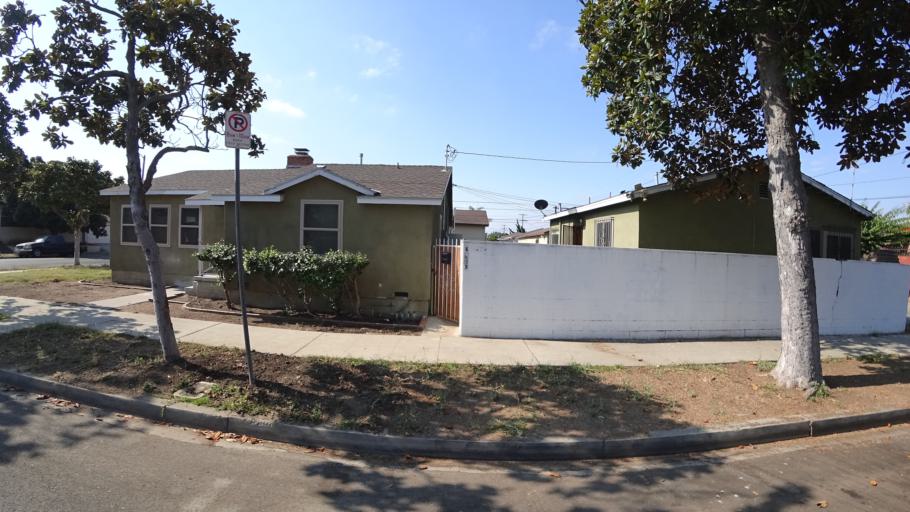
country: US
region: California
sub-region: Los Angeles County
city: Westmont
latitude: 33.9491
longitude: -118.3171
